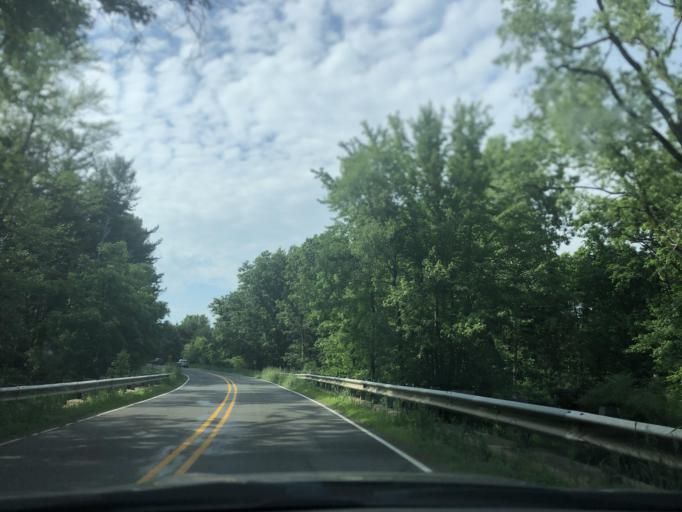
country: US
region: Michigan
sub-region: Clinton County
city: Bath
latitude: 42.8611
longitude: -84.4840
